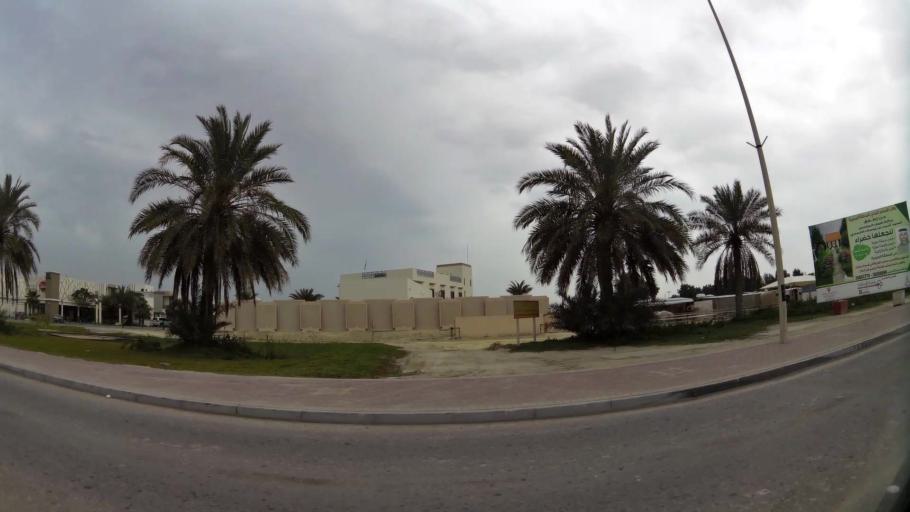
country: BH
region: Central Governorate
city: Dar Kulayb
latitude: 26.0515
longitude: 50.4876
